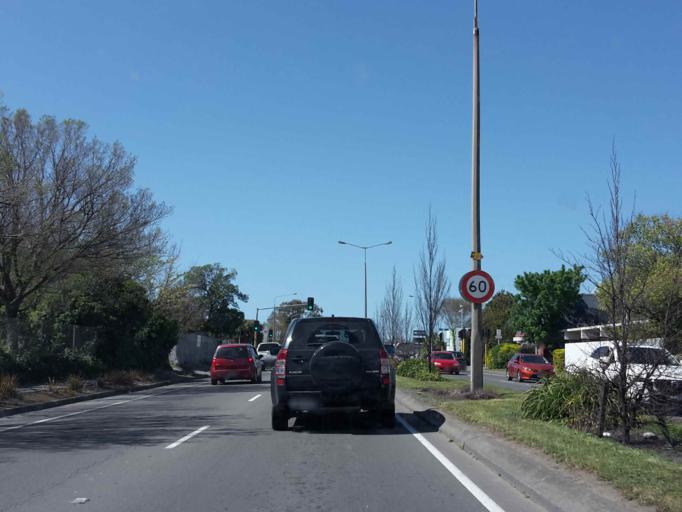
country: NZ
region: Canterbury
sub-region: Christchurch City
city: Christchurch
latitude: -43.5392
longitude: 172.5736
